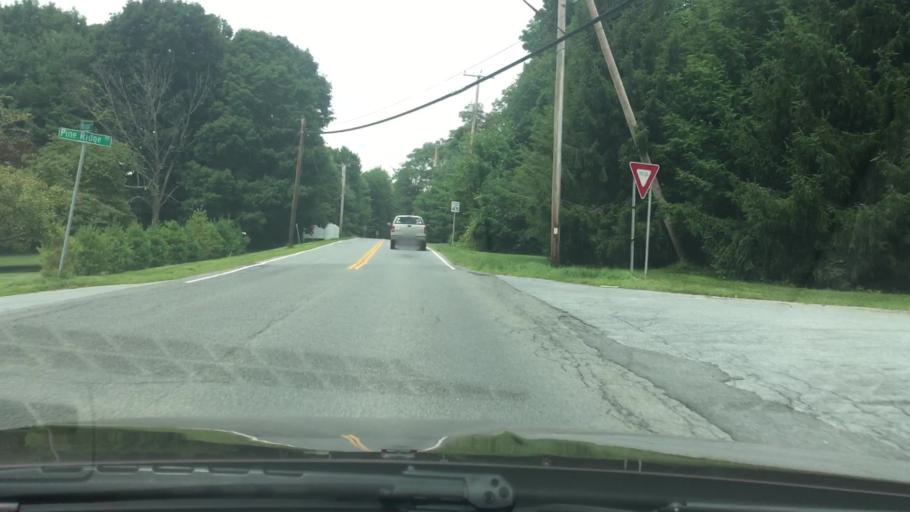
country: US
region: New York
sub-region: Dutchess County
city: Hillside Lake
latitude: 41.6475
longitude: -73.8227
